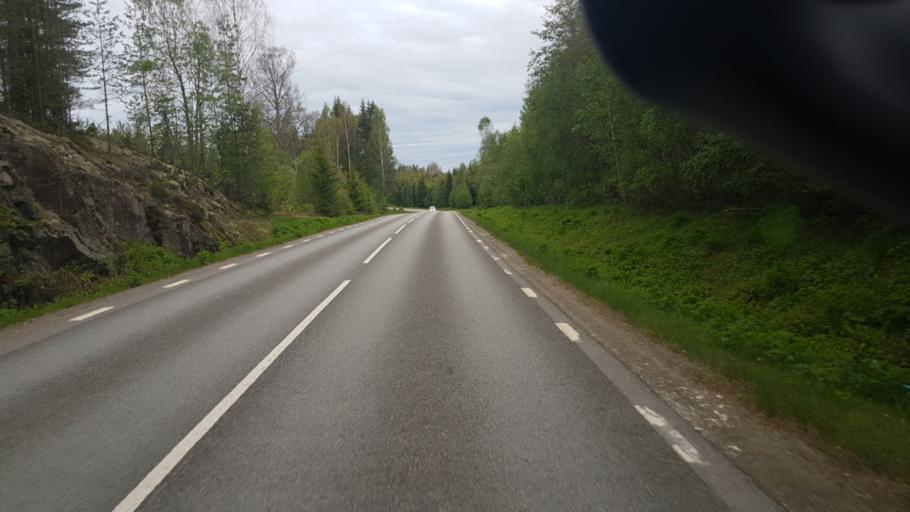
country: SE
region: Vaermland
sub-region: Arvika Kommun
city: Arvika
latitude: 59.7266
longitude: 12.5661
